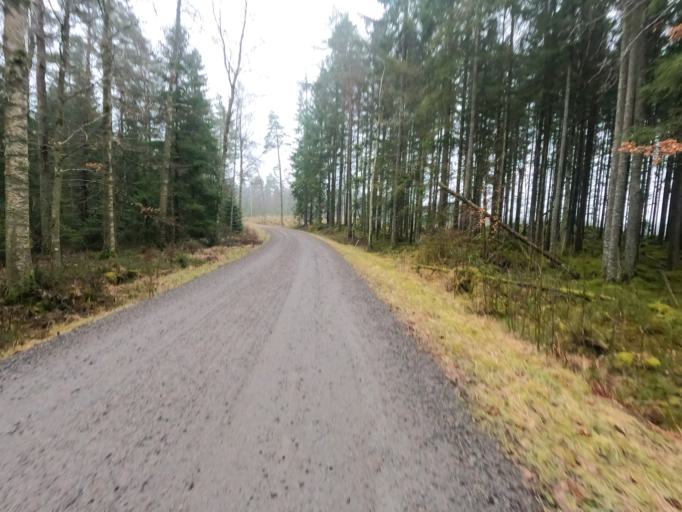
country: SE
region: Halland
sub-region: Hylte Kommun
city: Hyltebruk
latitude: 56.8075
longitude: 13.3213
